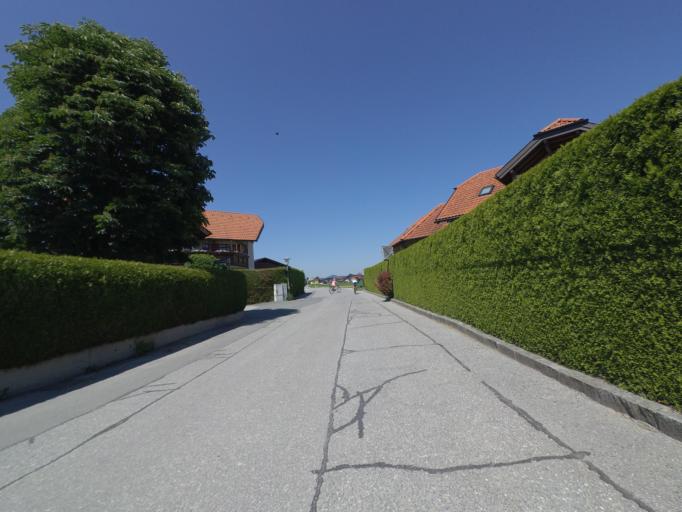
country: DE
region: Bavaria
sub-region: Upper Bavaria
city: Ainring
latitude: 47.7727
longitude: 12.9713
